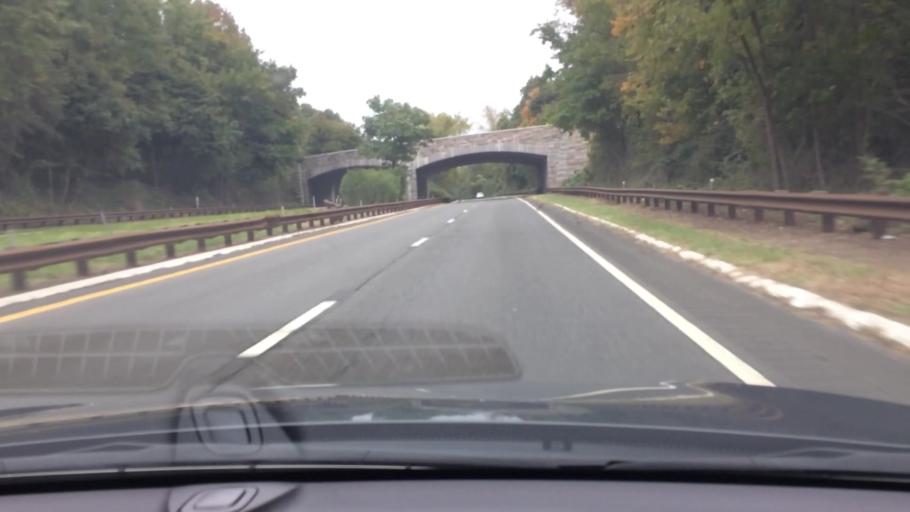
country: US
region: New York
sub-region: Rockland County
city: Sparkill
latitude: 41.0112
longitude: -73.9234
